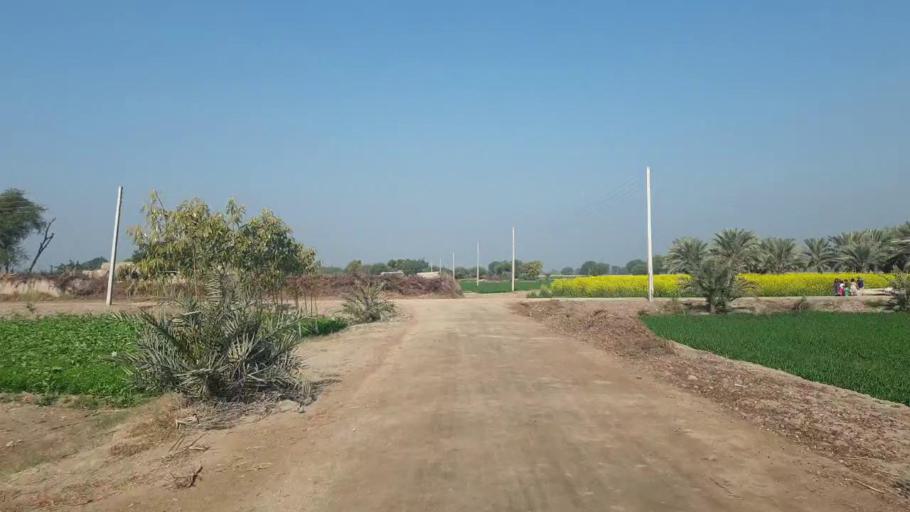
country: PK
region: Sindh
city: Shahdadpur
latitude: 25.9498
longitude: 68.5368
